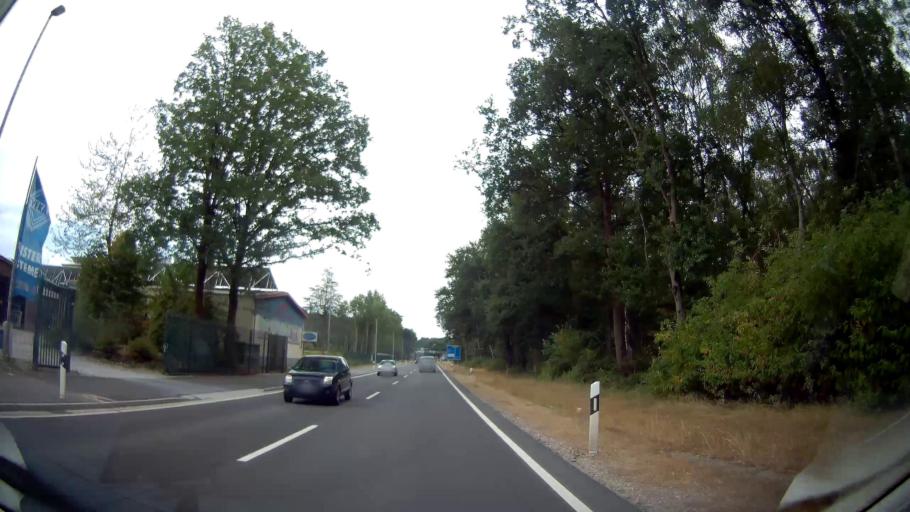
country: DE
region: North Rhine-Westphalia
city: Marl
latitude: 51.6762
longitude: 7.0757
